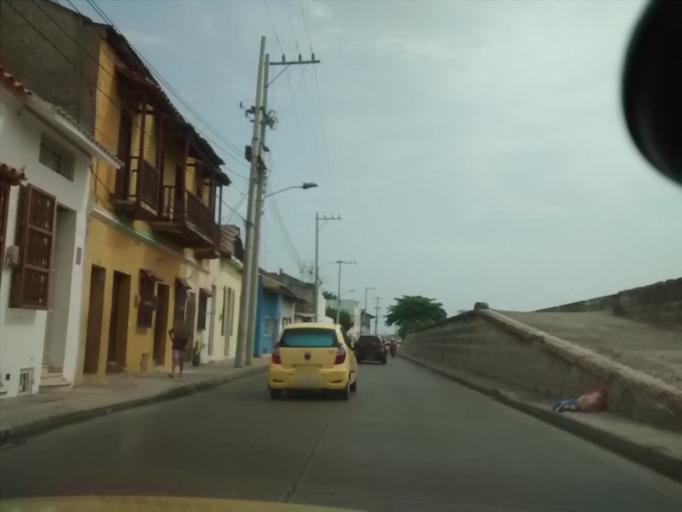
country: CO
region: Bolivar
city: Cartagena
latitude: 10.4206
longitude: -75.5439
